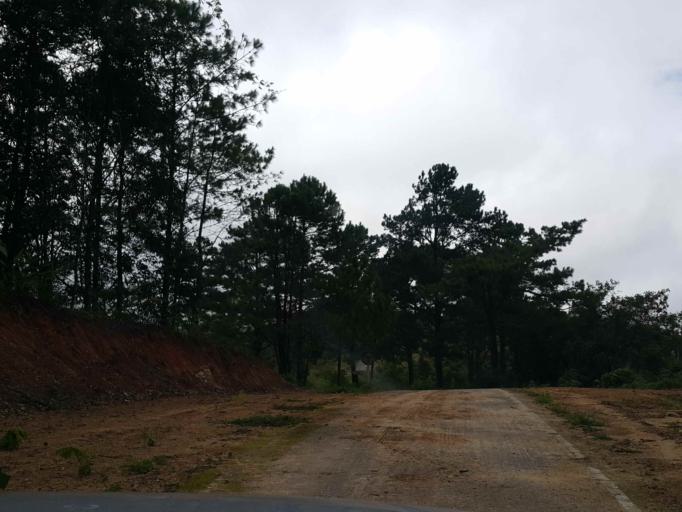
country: TH
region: Tak
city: Tak
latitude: 16.7827
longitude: 98.9272
